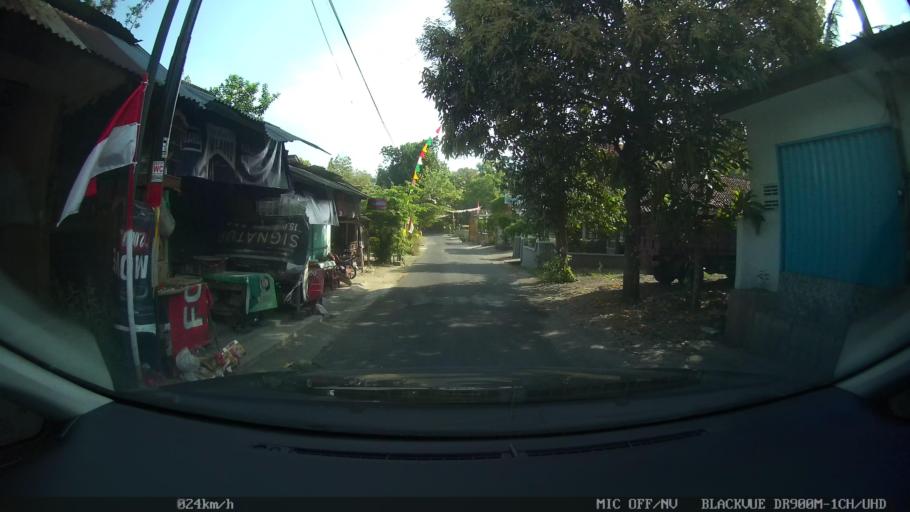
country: ID
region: Daerah Istimewa Yogyakarta
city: Kasihan
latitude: -7.8336
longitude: 110.3376
